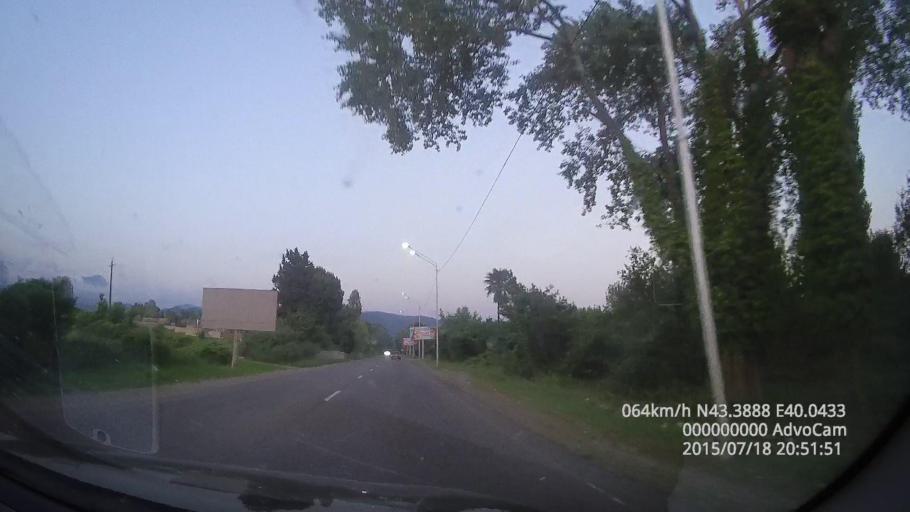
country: GE
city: Gantiadi
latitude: 43.3886
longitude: 40.0448
